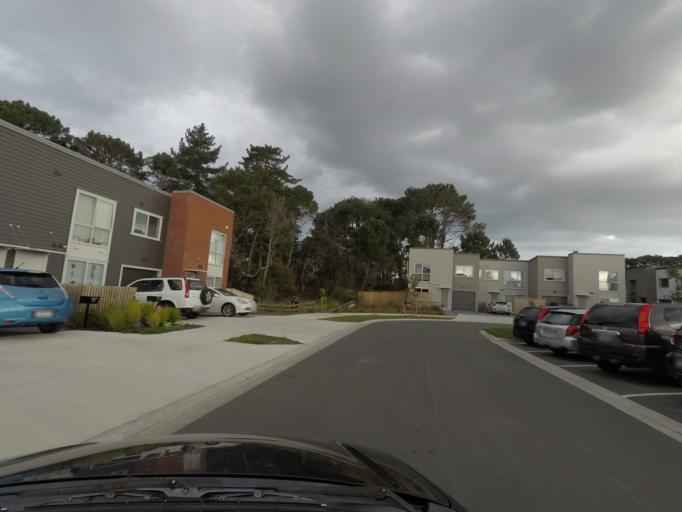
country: NZ
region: Auckland
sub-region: Auckland
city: Rosebank
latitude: -36.8262
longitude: 174.6280
